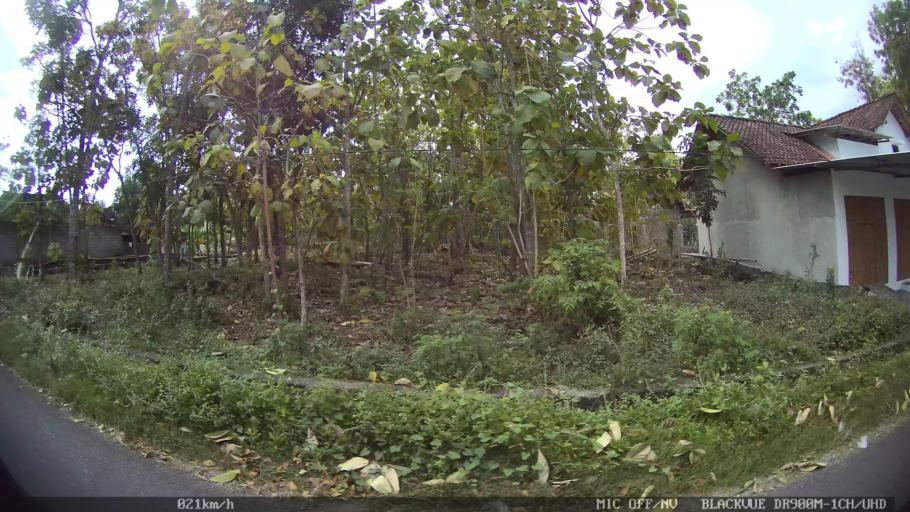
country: ID
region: Daerah Istimewa Yogyakarta
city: Kasihan
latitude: -7.8542
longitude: 110.3119
